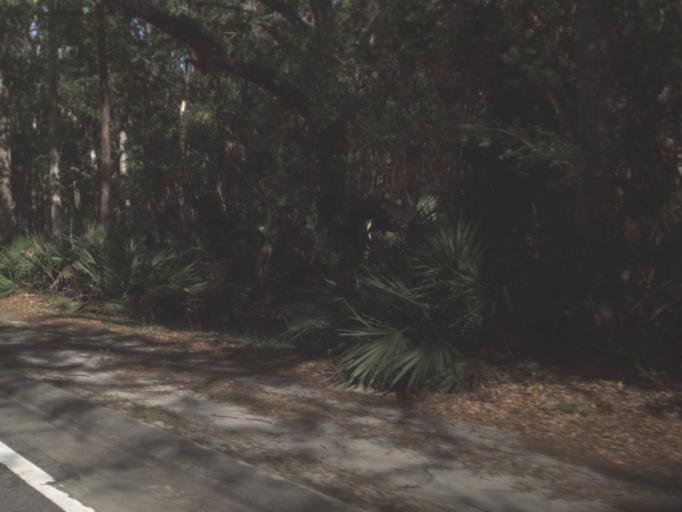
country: US
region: Florida
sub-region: Flagler County
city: Palm Coast
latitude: 29.5572
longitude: -81.1961
